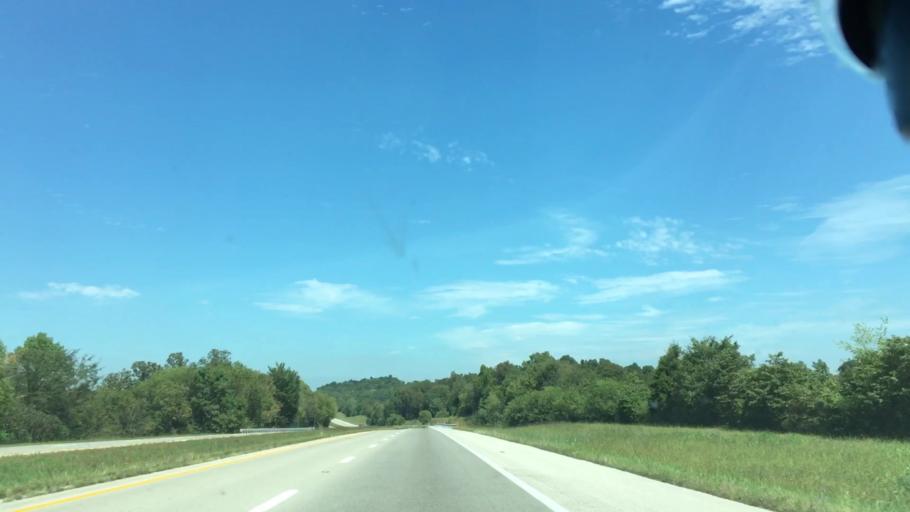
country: US
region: Kentucky
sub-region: Christian County
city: Hopkinsville
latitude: 36.9274
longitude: -87.4711
